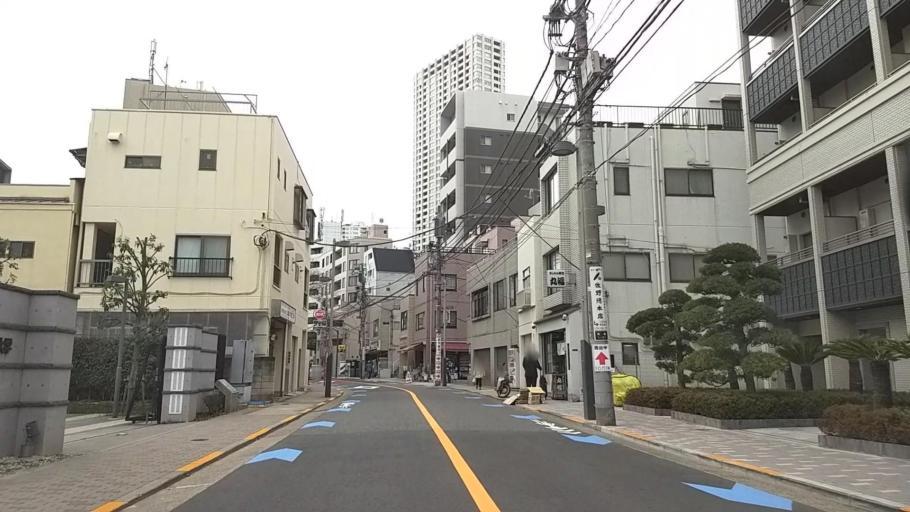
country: JP
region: Tokyo
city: Tokyo
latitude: 35.6383
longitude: 139.7341
